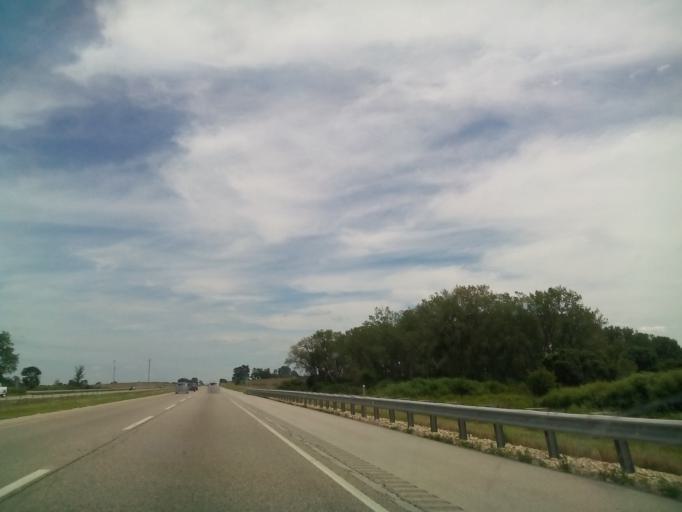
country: US
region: Illinois
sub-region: DeKalb County
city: Cortland
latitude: 41.9007
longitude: -88.6729
